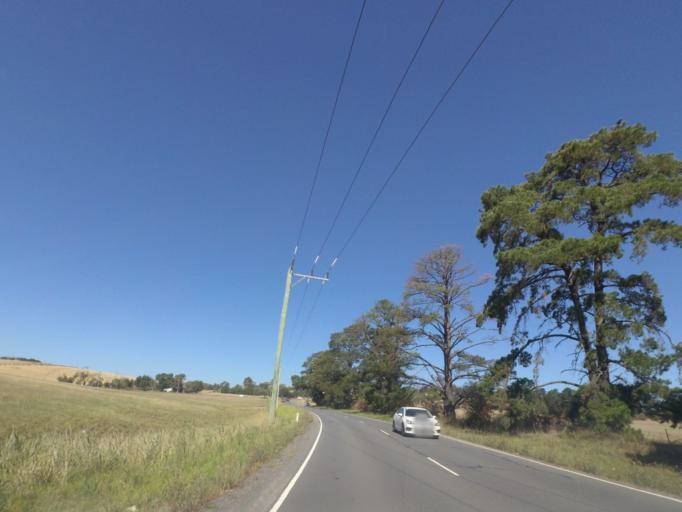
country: AU
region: Victoria
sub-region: Yarra Ranges
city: Chirnside Park
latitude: -37.7360
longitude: 145.3171
